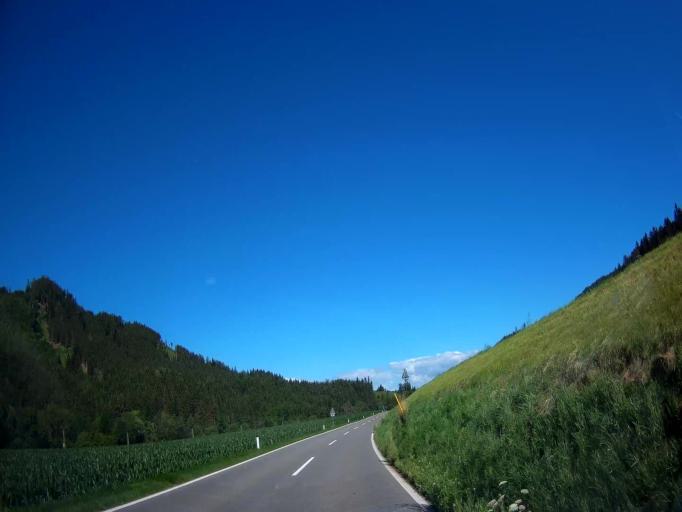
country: AT
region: Carinthia
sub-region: Politischer Bezirk Sankt Veit an der Glan
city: Bruckl
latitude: 46.7553
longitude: 14.4989
